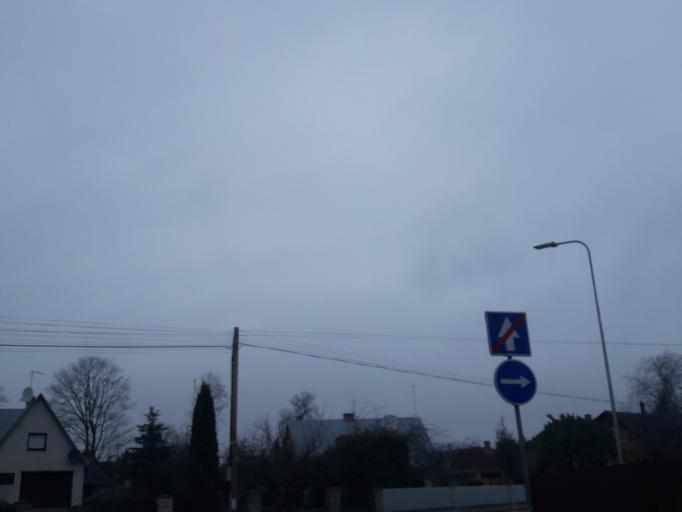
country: EE
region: Saare
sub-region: Kuressaare linn
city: Kuressaare
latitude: 58.2479
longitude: 22.4703
